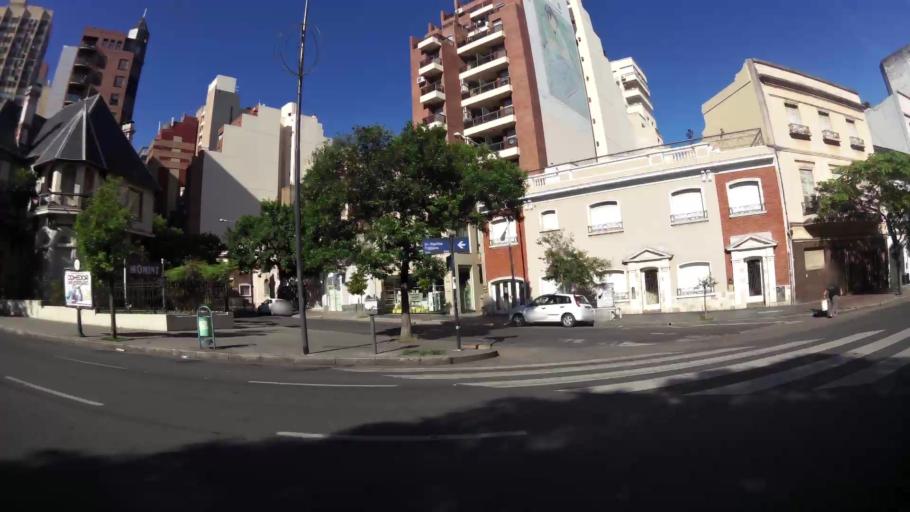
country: AR
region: Cordoba
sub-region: Departamento de Capital
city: Cordoba
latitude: -31.4272
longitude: -64.1856
